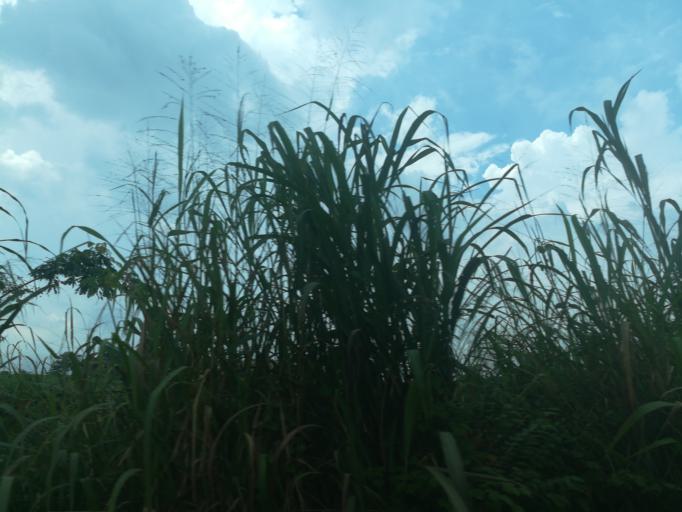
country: NG
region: Lagos
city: Ikorodu
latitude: 6.6678
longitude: 3.6416
